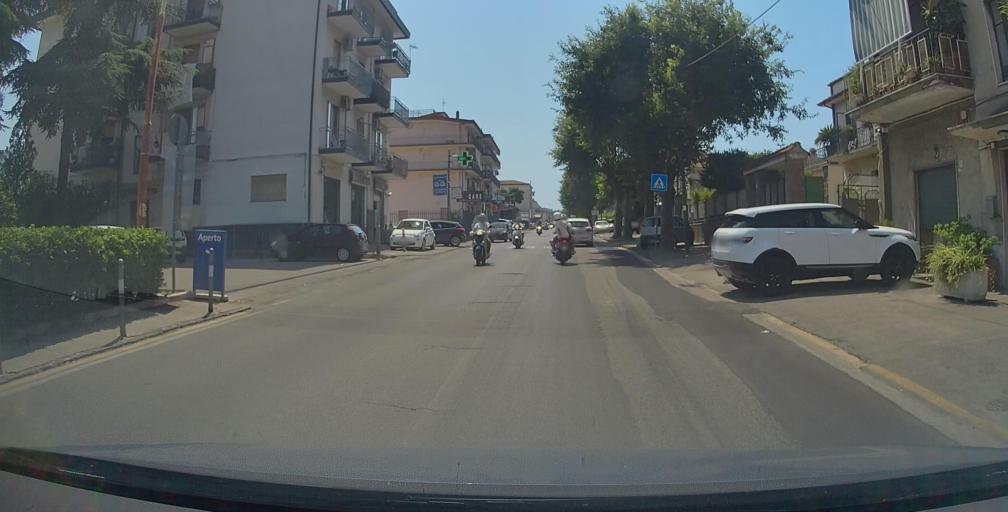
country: IT
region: Campania
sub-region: Provincia di Salerno
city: Cava De Tirreni
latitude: 40.7221
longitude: 14.6960
